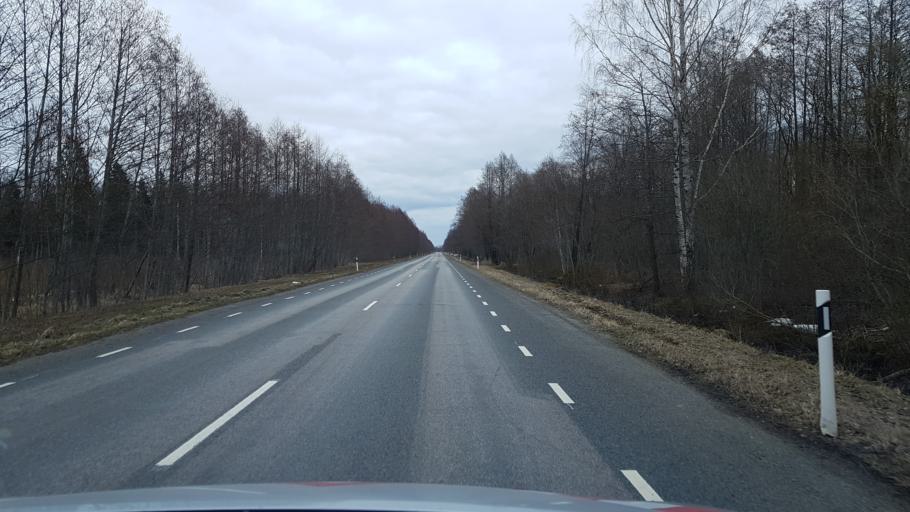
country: EE
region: Ida-Virumaa
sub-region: Narva-Joesuu linn
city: Narva-Joesuu
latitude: 59.3514
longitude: 28.0532
